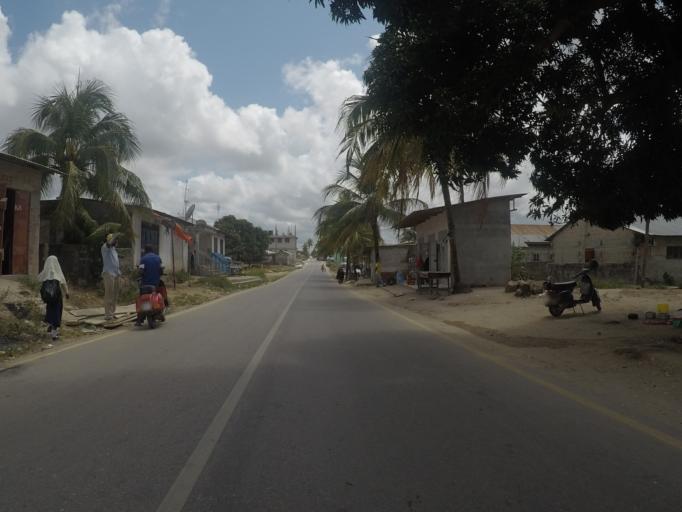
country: TZ
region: Zanzibar Urban/West
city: Zanzibar
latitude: -6.2006
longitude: 39.2435
